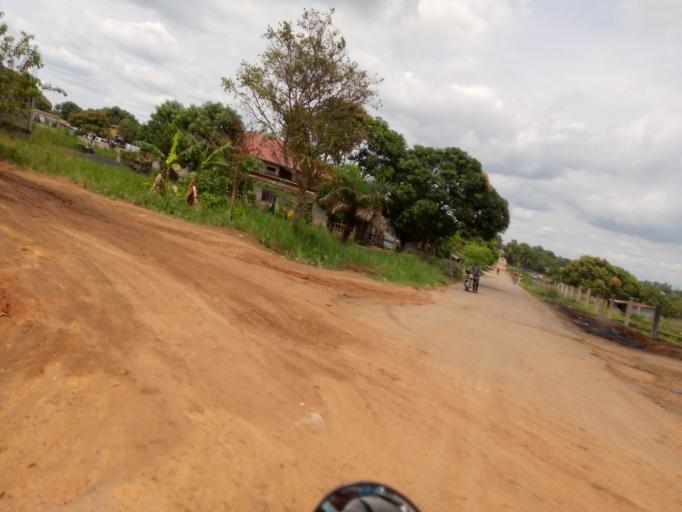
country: SL
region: Western Area
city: Waterloo
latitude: 8.3348
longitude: -13.0298
